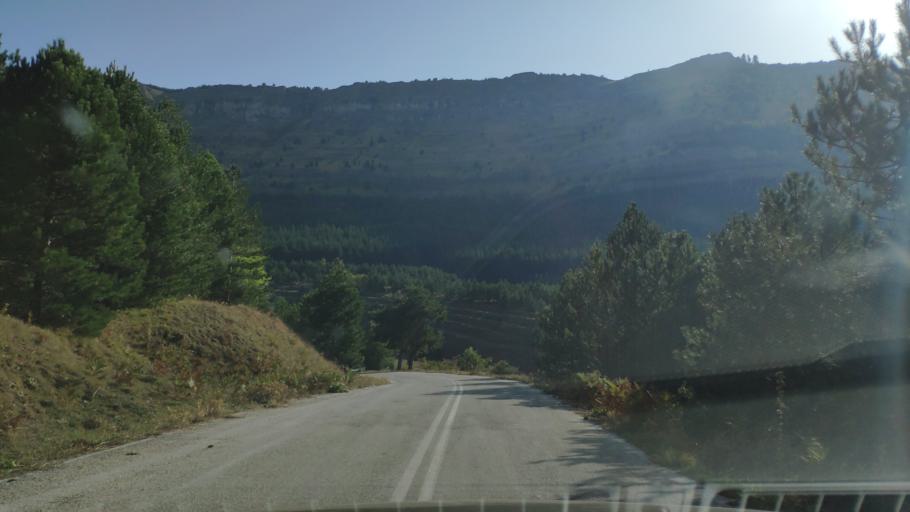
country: GR
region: West Greece
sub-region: Nomos Achaias
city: Aiyira
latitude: 38.0496
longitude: 22.3854
